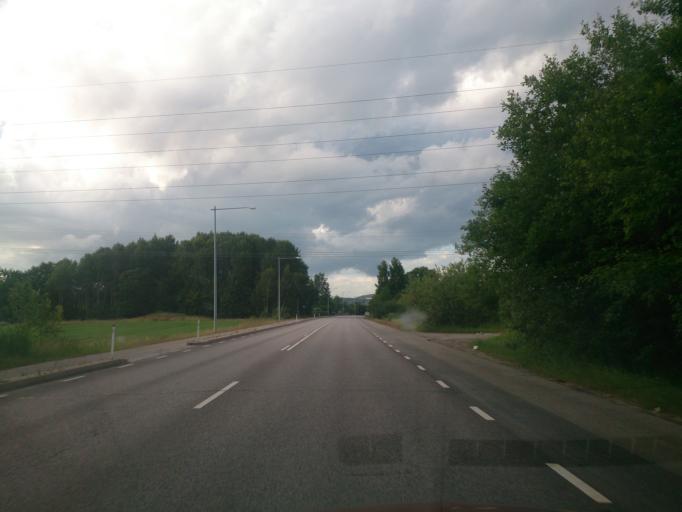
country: SE
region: OEstergoetland
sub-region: Norrkopings Kommun
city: Jursla
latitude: 58.6371
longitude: 16.1559
